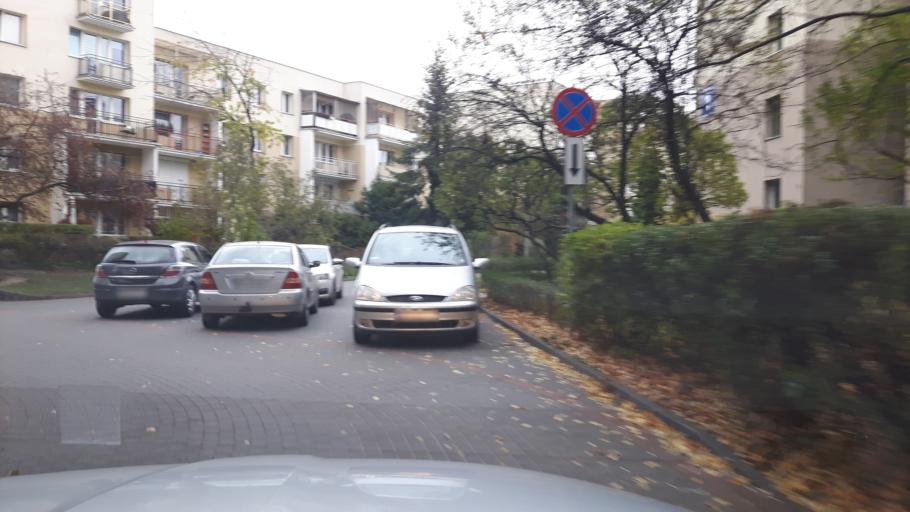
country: PL
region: Masovian Voivodeship
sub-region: Warszawa
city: Ursynow
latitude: 52.1548
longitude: 21.0270
